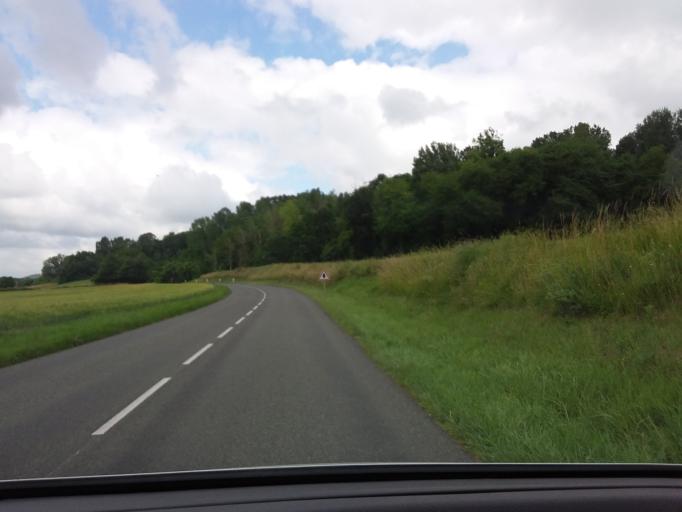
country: FR
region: Picardie
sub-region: Departement de l'Aisne
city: Vailly-sur-Aisne
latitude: 49.4052
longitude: 3.5391
